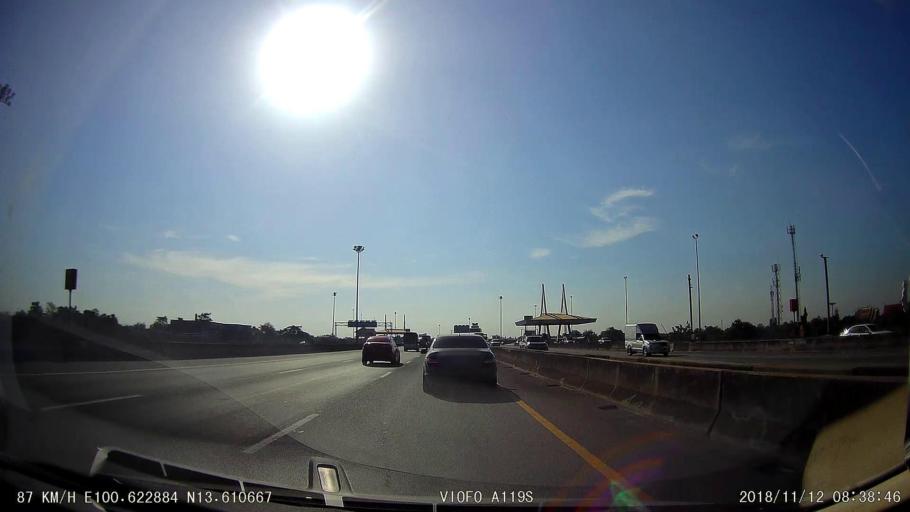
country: TH
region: Samut Prakan
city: Samut Prakan
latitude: 13.6101
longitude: 100.6234
